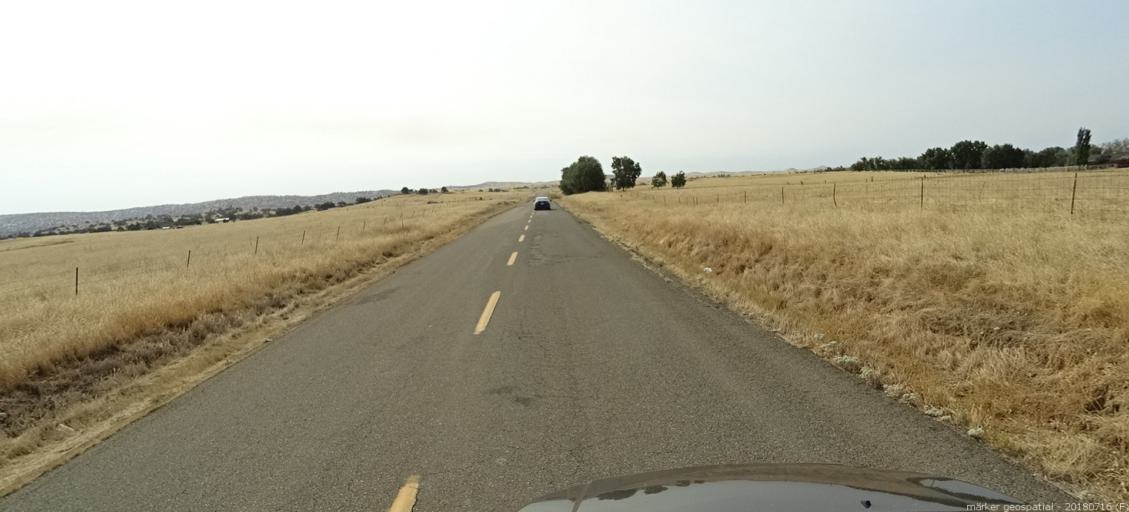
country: US
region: California
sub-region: Madera County
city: Bonadelle Ranchos-Madera Ranchos
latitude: 37.1146
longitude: -119.9203
